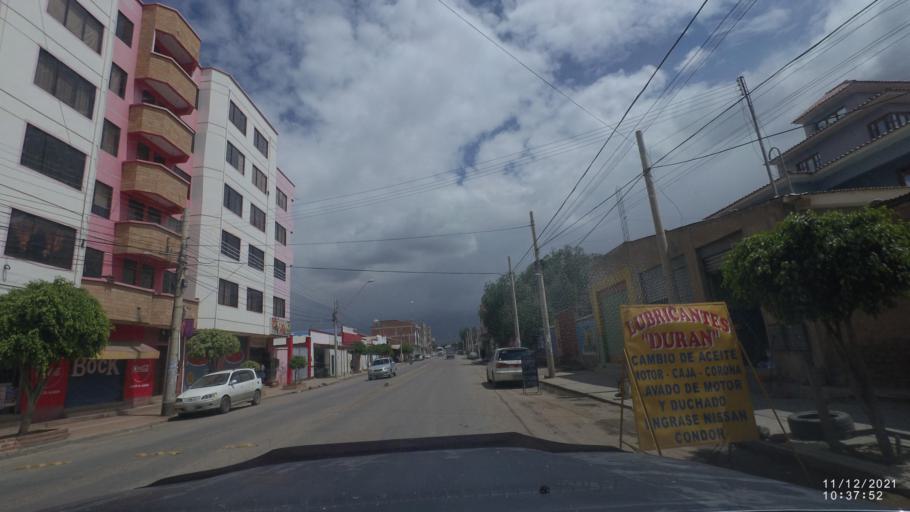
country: BO
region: Cochabamba
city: Cochabamba
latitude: -17.4427
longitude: -66.1250
